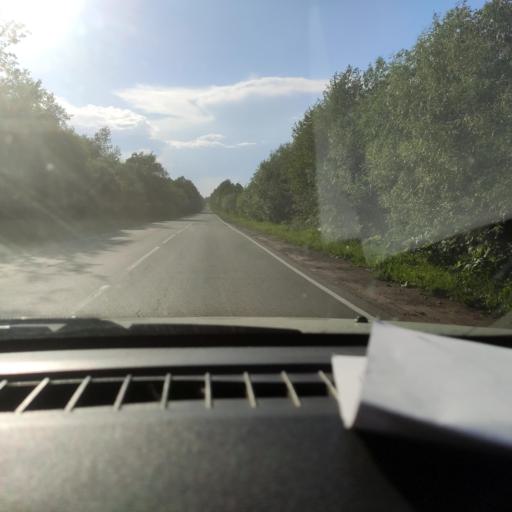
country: RU
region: Perm
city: Krasnokamsk
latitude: 58.1286
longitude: 55.7925
